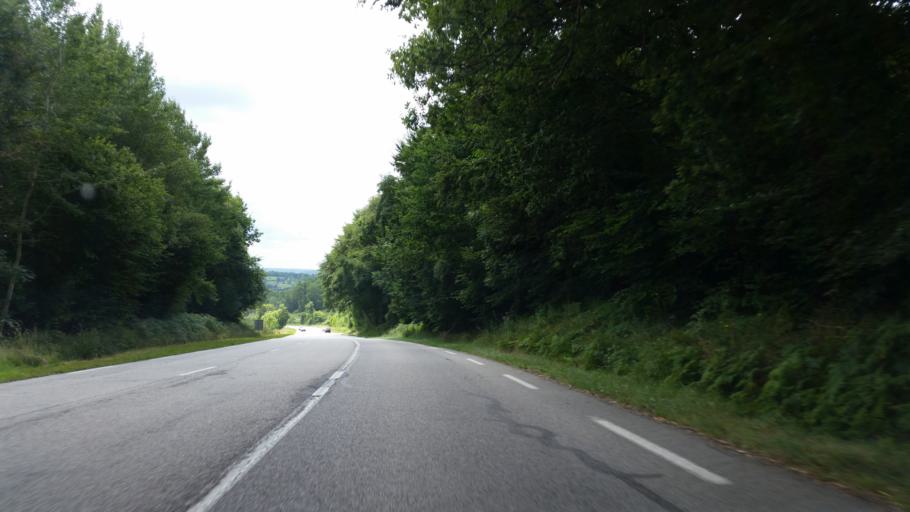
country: FR
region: Lower Normandy
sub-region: Departement du Calvados
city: Saint-Gatien-des-Bois
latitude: 49.3336
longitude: 0.2034
